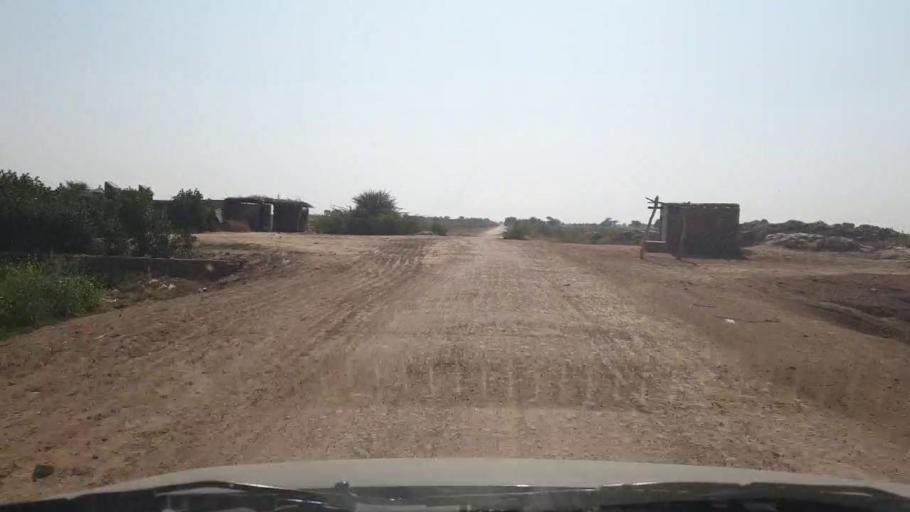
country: PK
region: Sindh
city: Samaro
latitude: 25.1874
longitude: 69.3393
